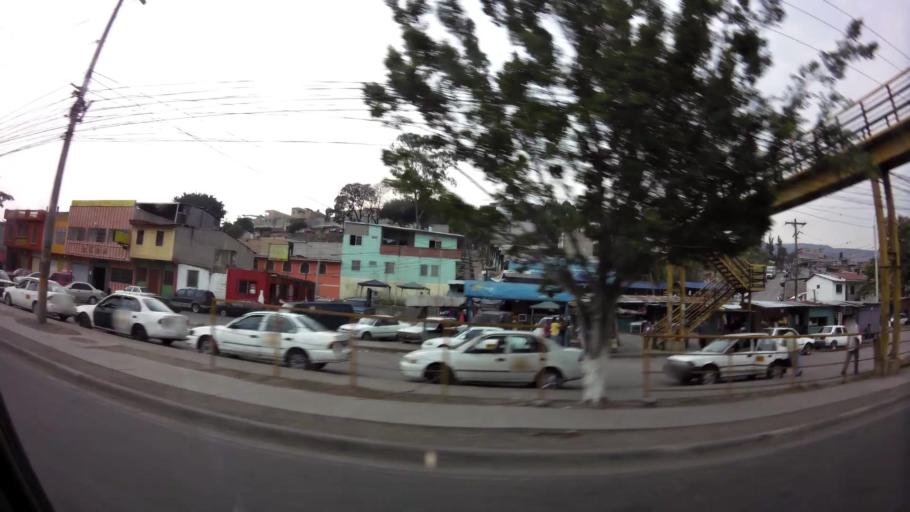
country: HN
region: Francisco Morazan
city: Tegucigalpa
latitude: 14.0920
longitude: -87.2390
